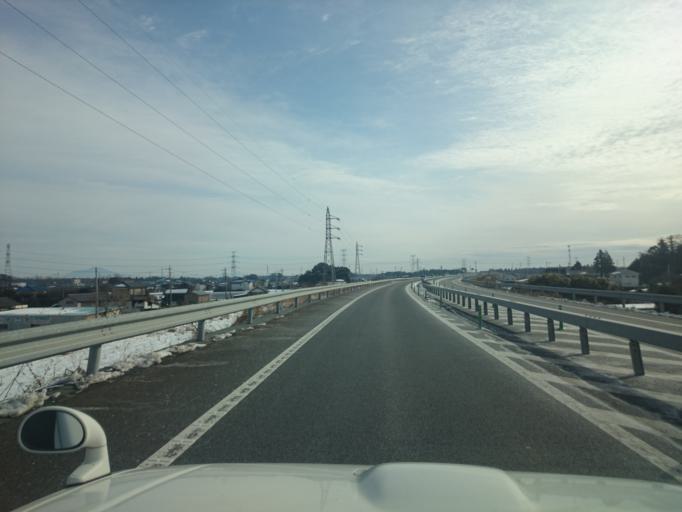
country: JP
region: Ibaraki
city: Sakai
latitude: 36.1282
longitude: 139.7954
